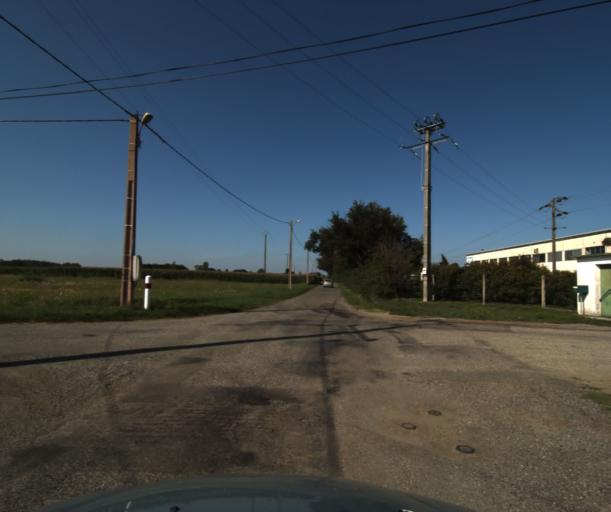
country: FR
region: Midi-Pyrenees
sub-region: Departement de la Haute-Garonne
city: Le Fauga
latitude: 43.4216
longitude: 1.3077
